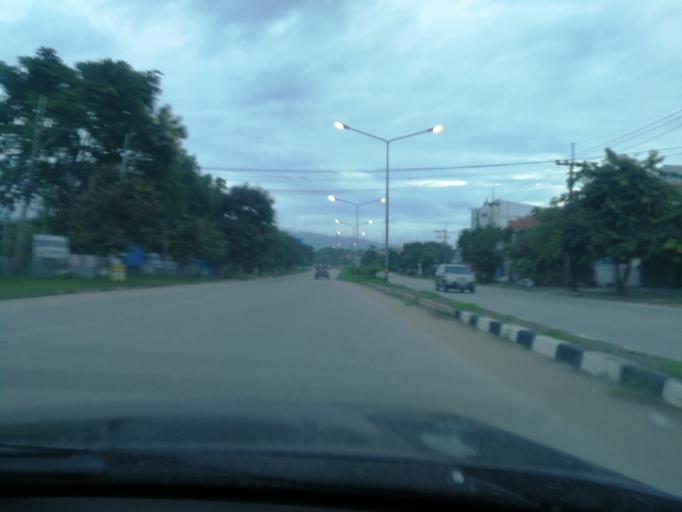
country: TH
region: Chiang Mai
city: Hot
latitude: 18.1855
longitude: 98.6127
